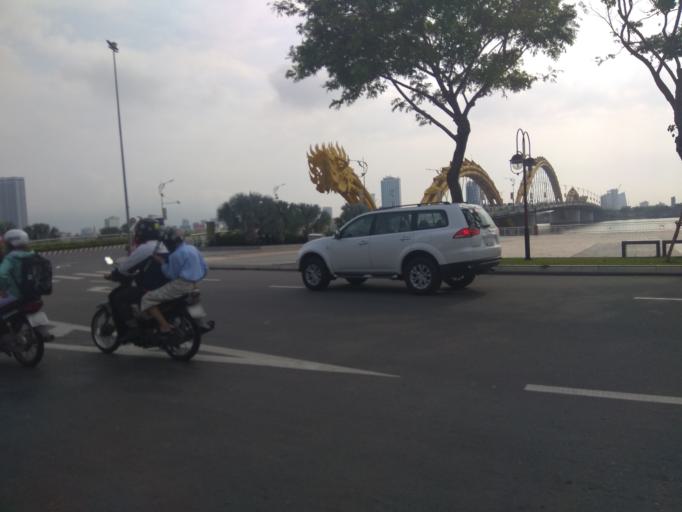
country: VN
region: Da Nang
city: Da Nang
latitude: 16.0606
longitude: 108.2240
